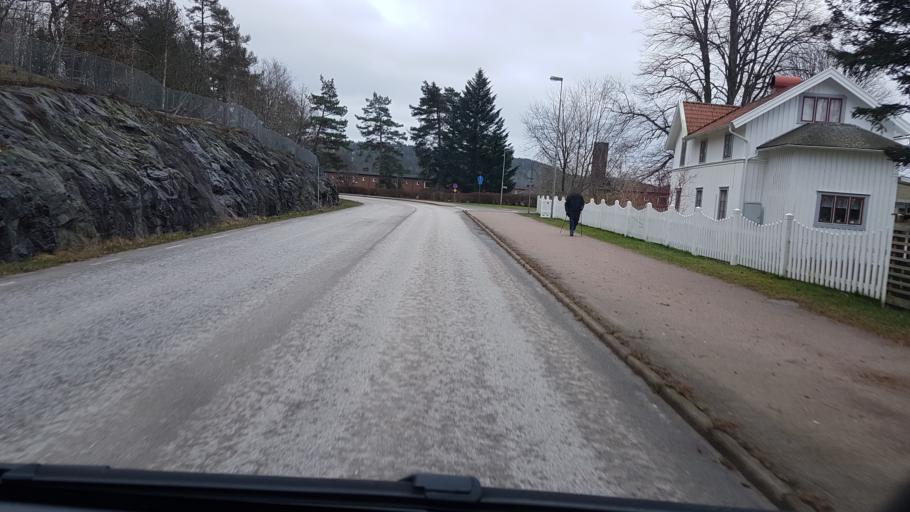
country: SE
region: Vaestra Goetaland
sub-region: Lerums Kommun
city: Stenkullen
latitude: 57.7912
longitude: 12.3085
